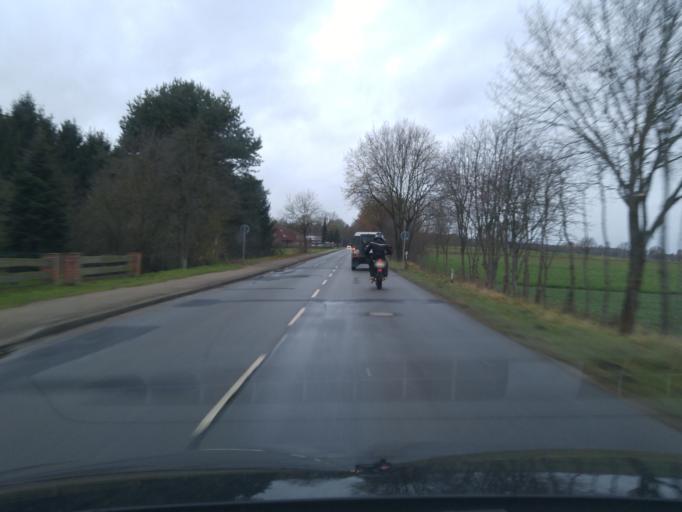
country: DE
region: Lower Saxony
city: Rullstorf
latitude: 53.2719
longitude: 10.5136
